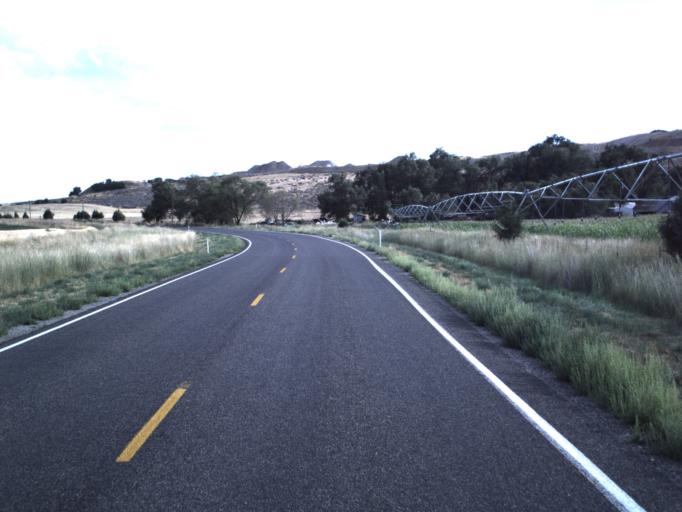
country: US
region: Utah
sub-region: Cache County
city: Benson
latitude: 41.8832
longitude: -111.9516
